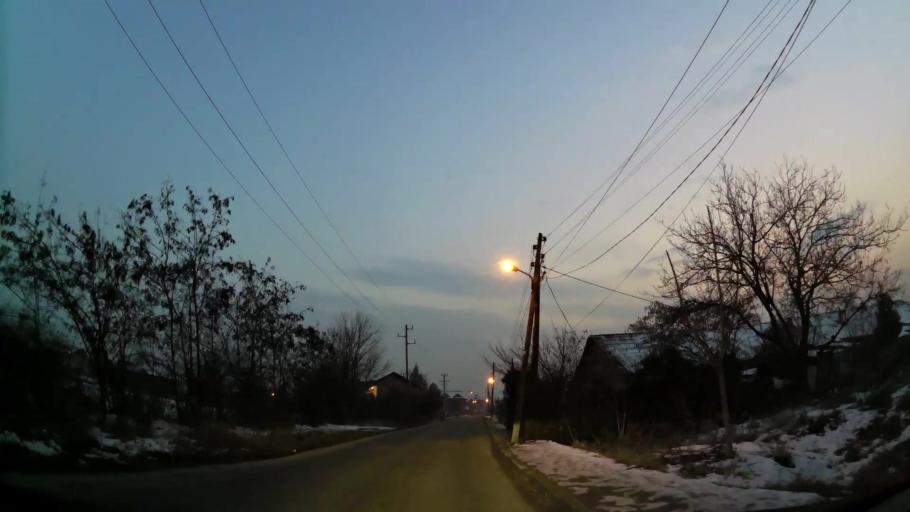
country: MK
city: Creshevo
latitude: 42.0050
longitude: 21.5173
